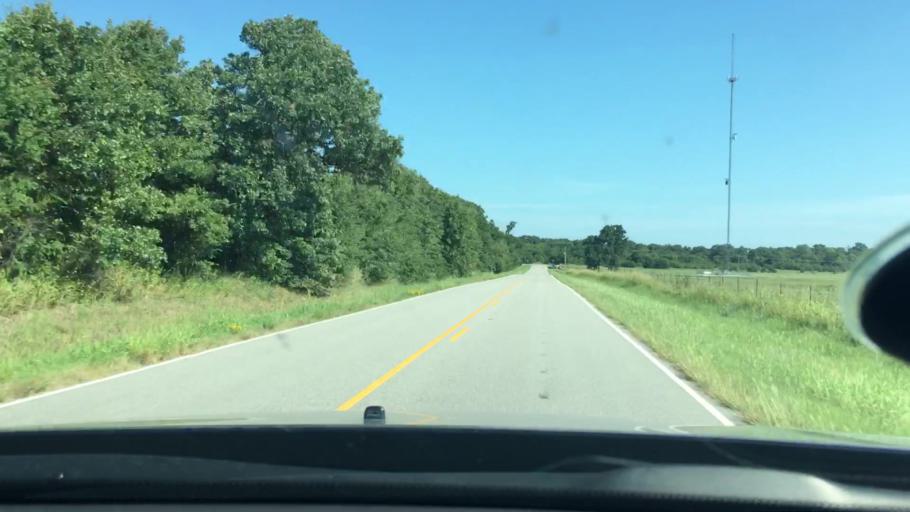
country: US
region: Oklahoma
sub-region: Johnston County
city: Tishomingo
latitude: 34.3570
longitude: -96.5488
